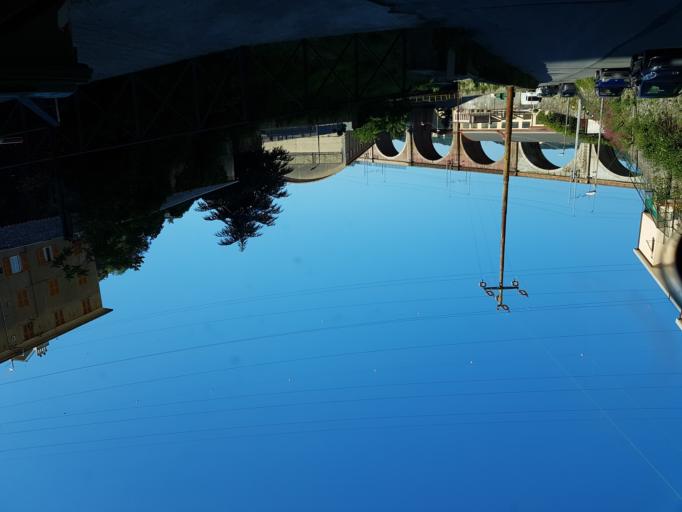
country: IT
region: Liguria
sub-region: Provincia di Genova
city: Genoa
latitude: 44.4553
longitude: 8.8892
